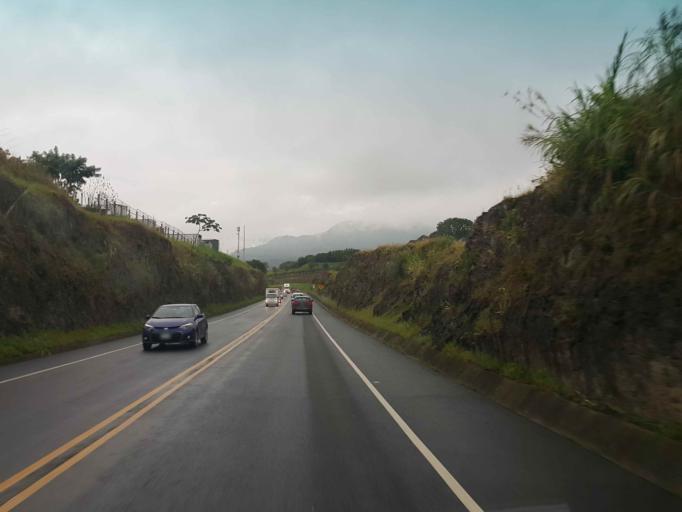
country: CR
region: Heredia
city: Colon
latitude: 9.9456
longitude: -84.2307
